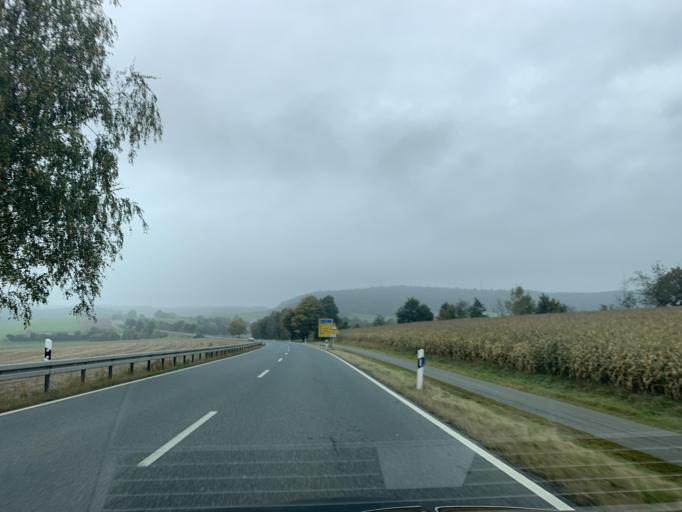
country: DE
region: Bavaria
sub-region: Upper Palatinate
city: Gleiritsch
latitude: 49.4764
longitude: 12.3152
